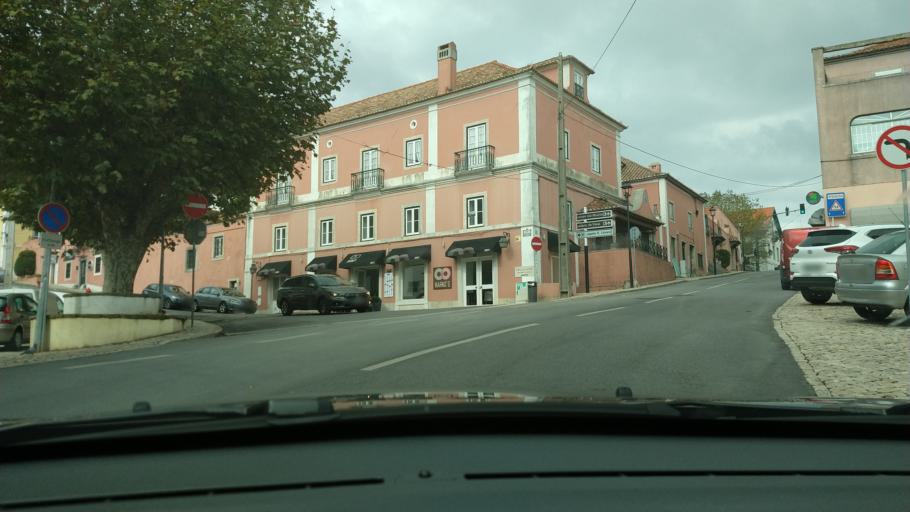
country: PT
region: Lisbon
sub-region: Sintra
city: Sintra
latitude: 38.7909
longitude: -9.3801
